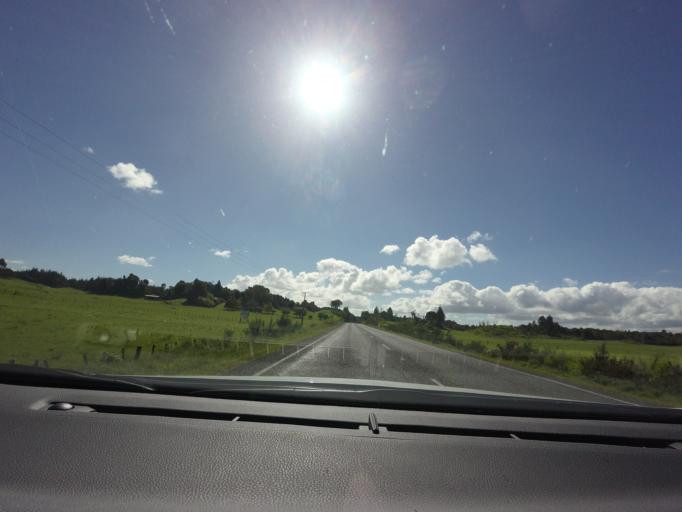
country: NZ
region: Bay of Plenty
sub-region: Rotorua District
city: Rotorua
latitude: -38.0414
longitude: 176.0587
